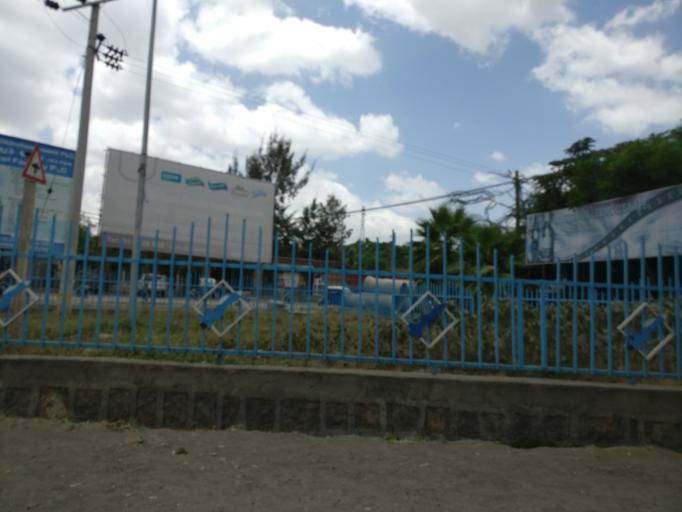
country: ET
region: Oromiya
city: Bishoftu
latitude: 8.7536
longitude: 38.9542
